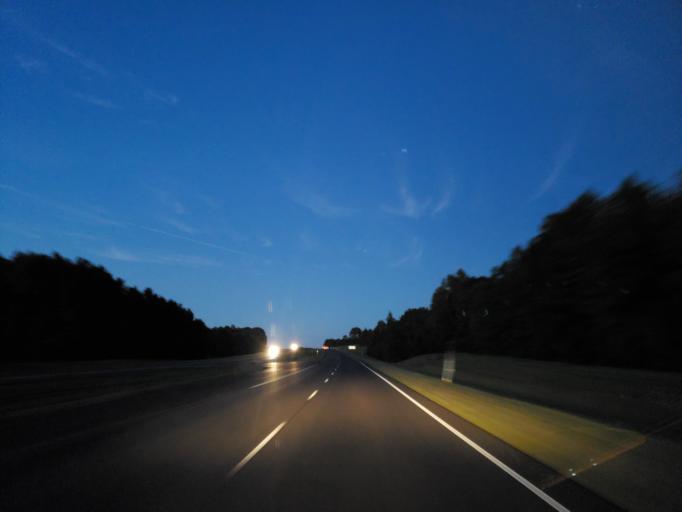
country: US
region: Mississippi
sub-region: Clarke County
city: Quitman
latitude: 32.0021
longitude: -88.6928
